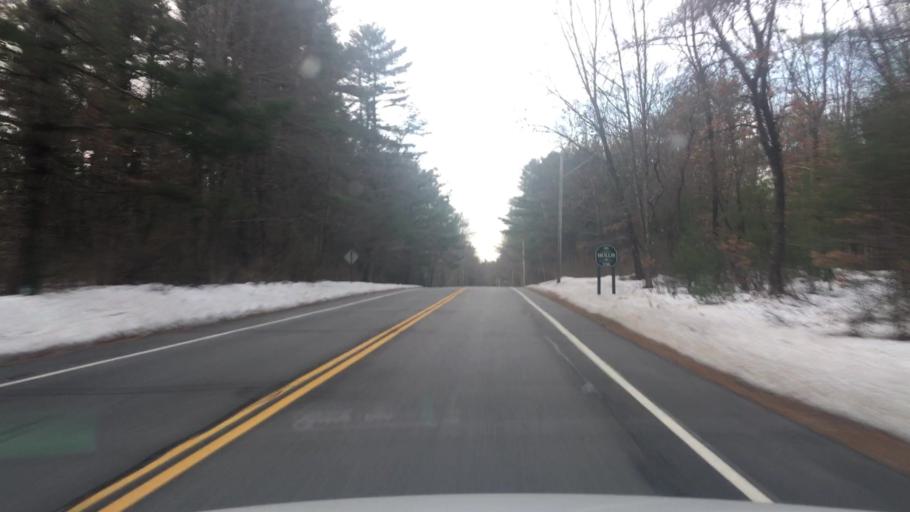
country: US
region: Maine
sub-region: York County
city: Dayton
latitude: 43.5621
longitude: -70.6197
